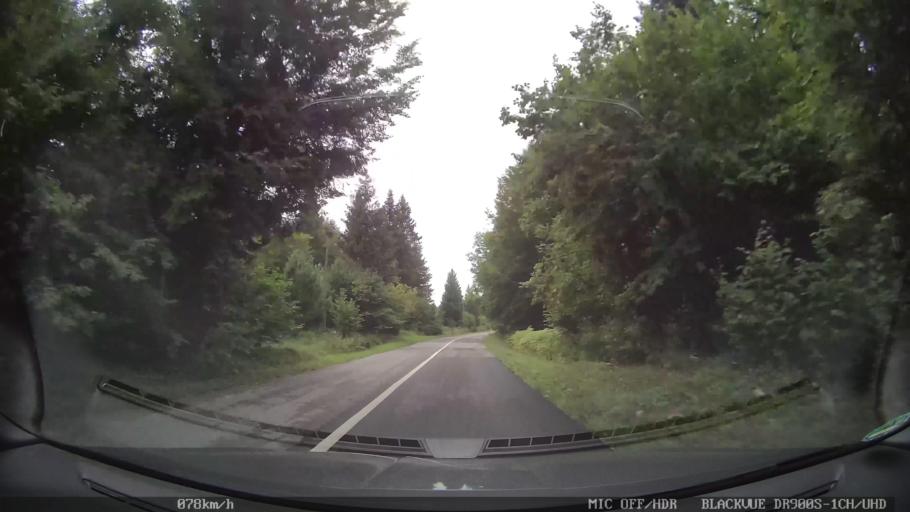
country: HR
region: Licko-Senjska
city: Jezerce
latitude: 44.9526
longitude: 15.5303
